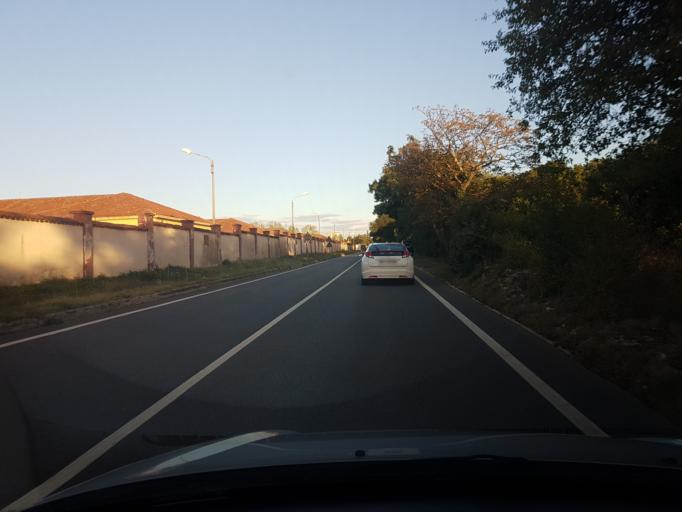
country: IT
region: Friuli Venezia Giulia
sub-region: Provincia di Trieste
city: Villa Opicina
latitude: 45.6964
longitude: 13.7772
